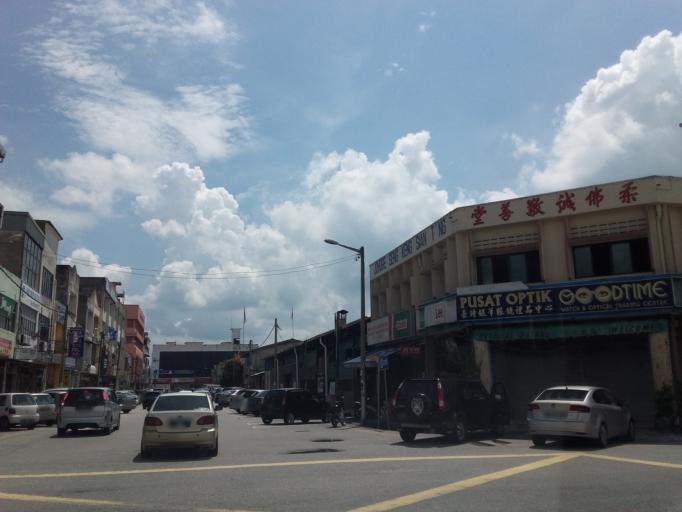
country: MY
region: Johor
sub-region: Daerah Batu Pahat
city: Batu Pahat
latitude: 1.8527
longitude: 102.9276
